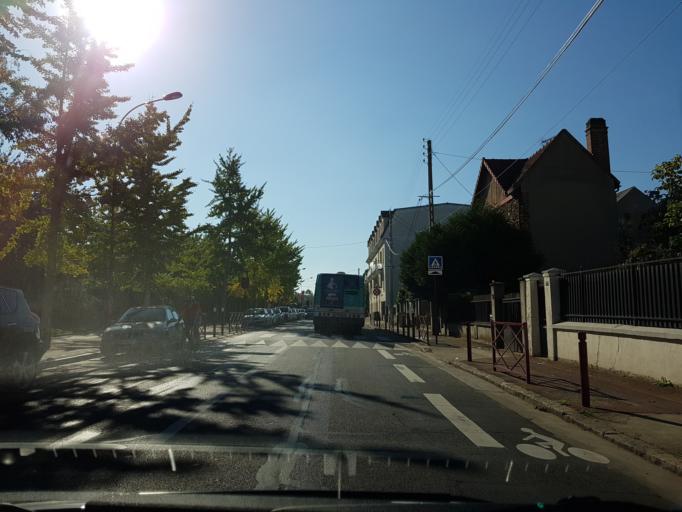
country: FR
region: Ile-de-France
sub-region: Departement du Val-de-Marne
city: Fresnes
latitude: 48.7629
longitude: 2.3182
